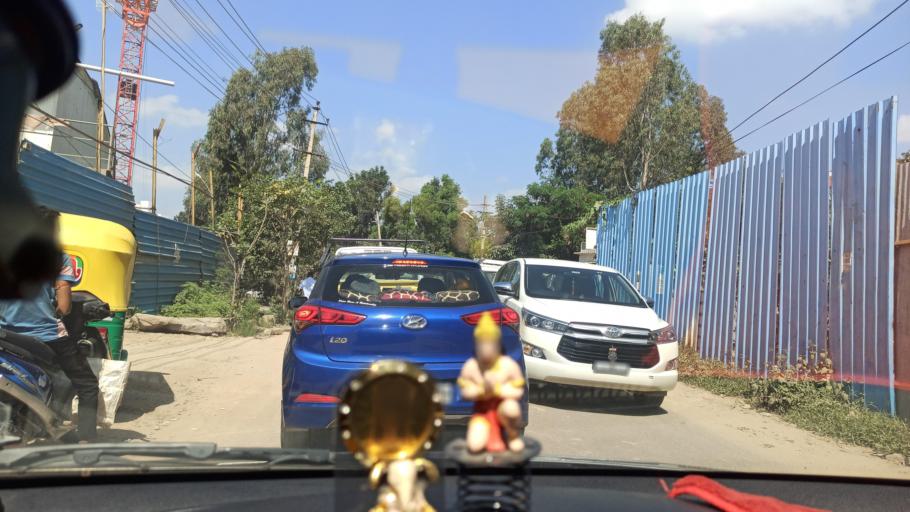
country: IN
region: Karnataka
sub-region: Bangalore Urban
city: Bangalore
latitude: 12.9727
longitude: 77.7076
